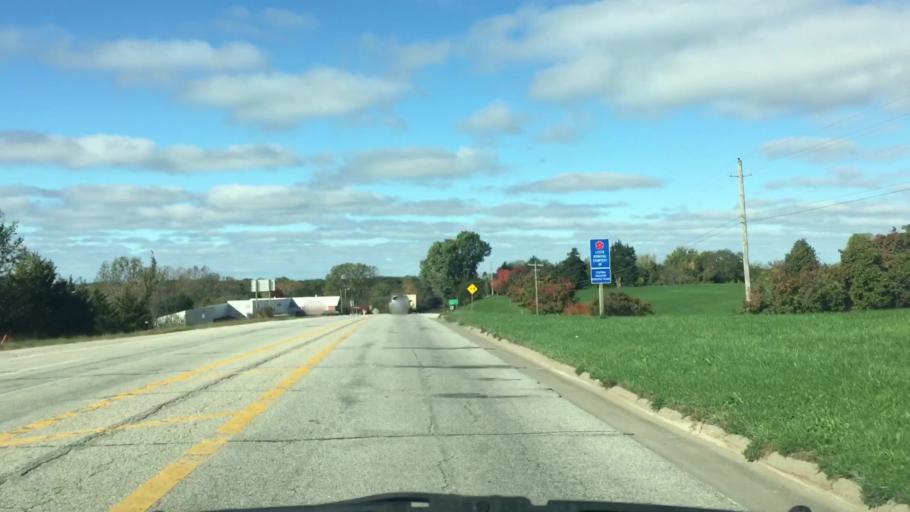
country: US
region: Iowa
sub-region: Decatur County
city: Leon
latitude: 40.7397
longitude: -93.7618
